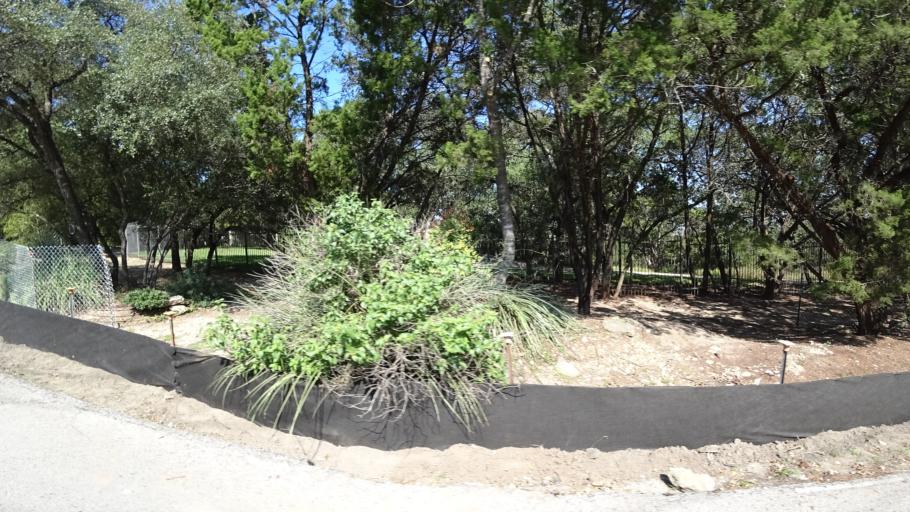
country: US
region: Texas
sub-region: Travis County
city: West Lake Hills
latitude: 30.2983
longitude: -97.8088
